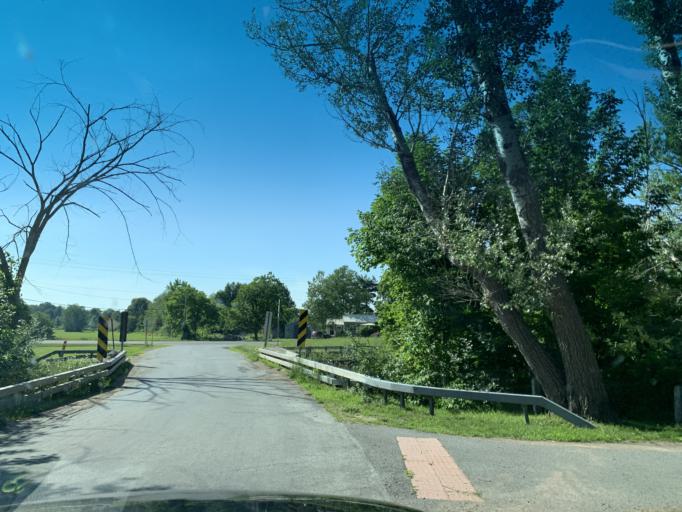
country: US
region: New York
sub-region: Madison County
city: Oneida
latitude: 43.1562
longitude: -75.6702
